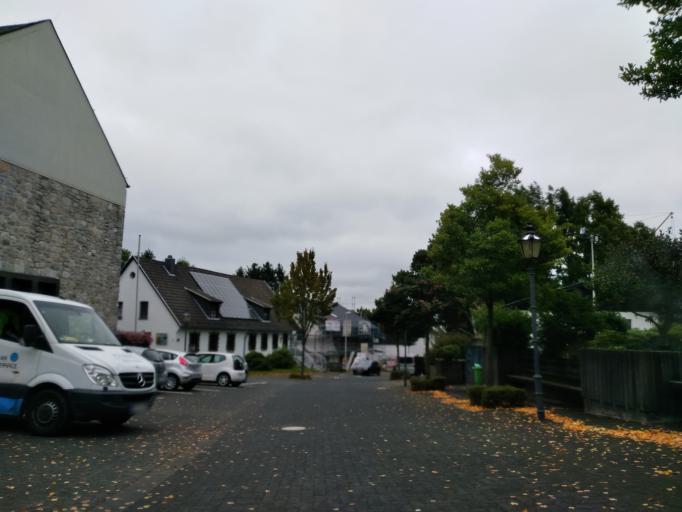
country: DE
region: North Rhine-Westphalia
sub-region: Regierungsbezirk Koln
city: Bad Honnef
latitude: 50.6812
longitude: 7.2687
